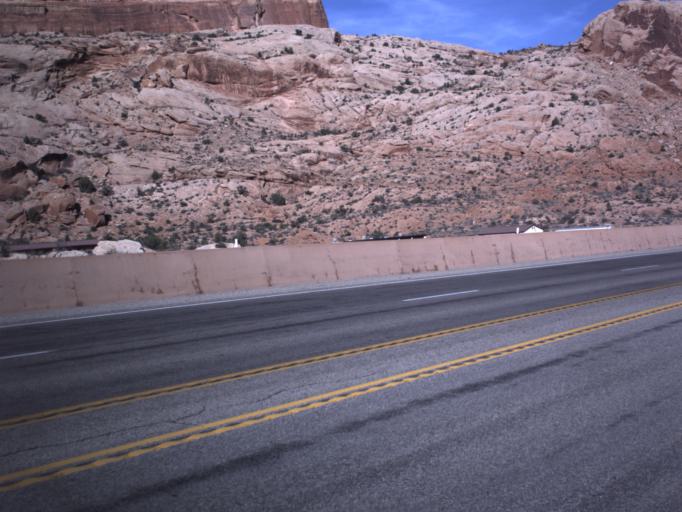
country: US
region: Utah
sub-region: Grand County
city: Moab
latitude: 38.6154
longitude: -109.6154
